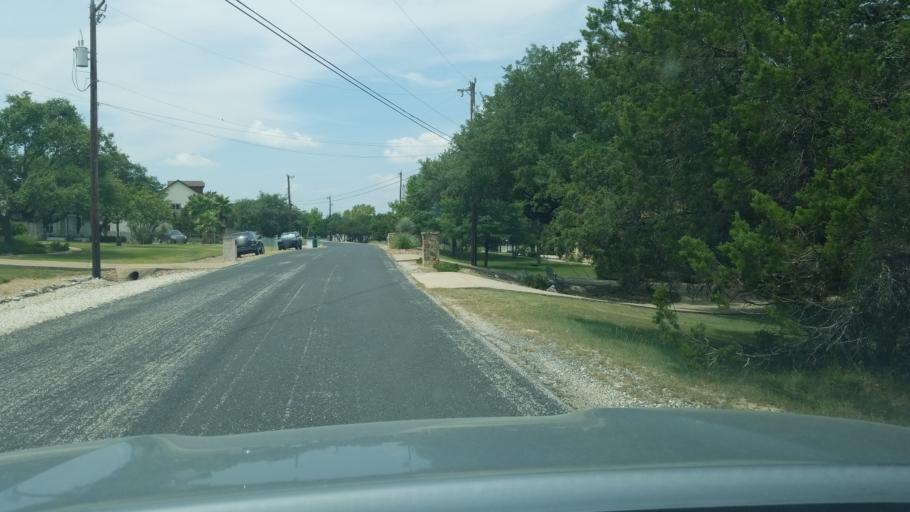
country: US
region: Texas
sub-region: Bexar County
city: Timberwood Park
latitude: 29.6882
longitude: -98.5056
